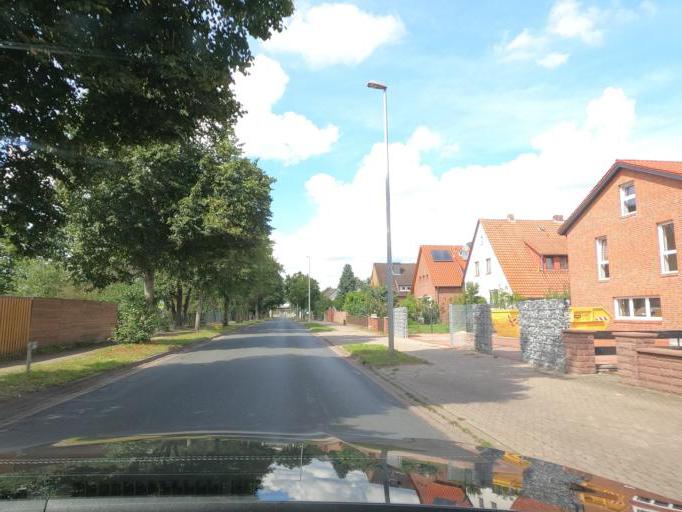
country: DE
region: Lower Saxony
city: Isernhagen Farster Bauerschaft
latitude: 52.5118
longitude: 9.8733
